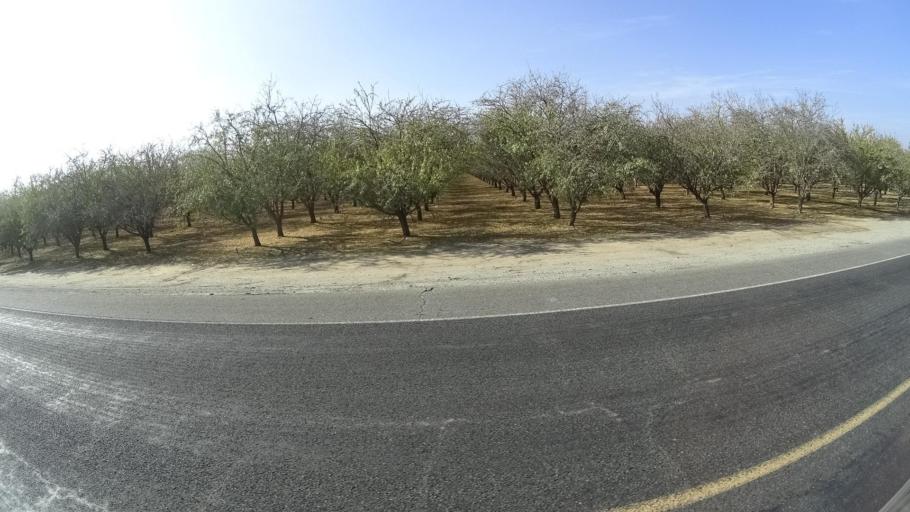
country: US
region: California
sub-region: Kern County
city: McFarland
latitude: 35.6497
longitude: -119.1956
